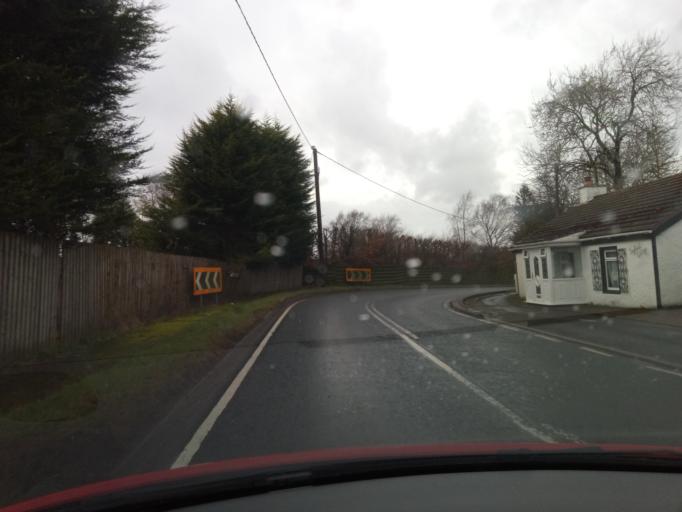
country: GB
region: Scotland
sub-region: East Dunbartonshire
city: Kirkintilloch
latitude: 55.9191
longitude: -4.1775
